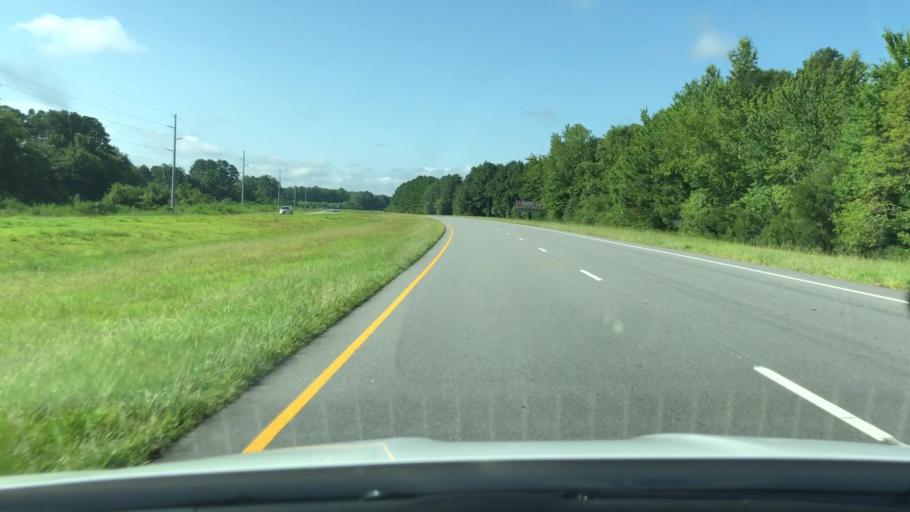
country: US
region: North Carolina
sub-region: Pasquotank County
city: Elizabeth City
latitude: 36.4439
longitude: -76.3391
